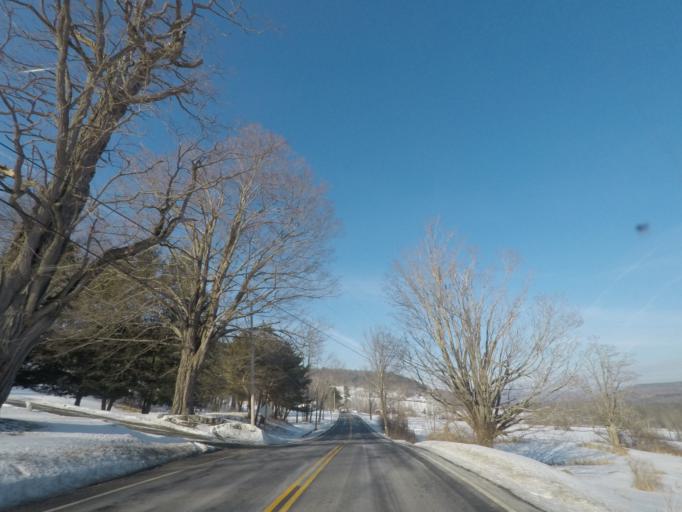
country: US
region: Massachusetts
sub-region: Berkshire County
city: Richmond
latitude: 42.4924
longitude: -73.3870
